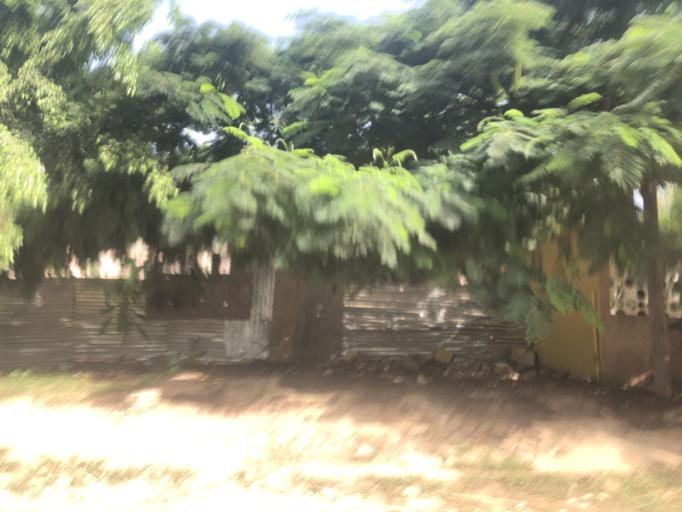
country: SN
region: Dakar
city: Mermoz Boabab
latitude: 14.7312
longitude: -17.4986
